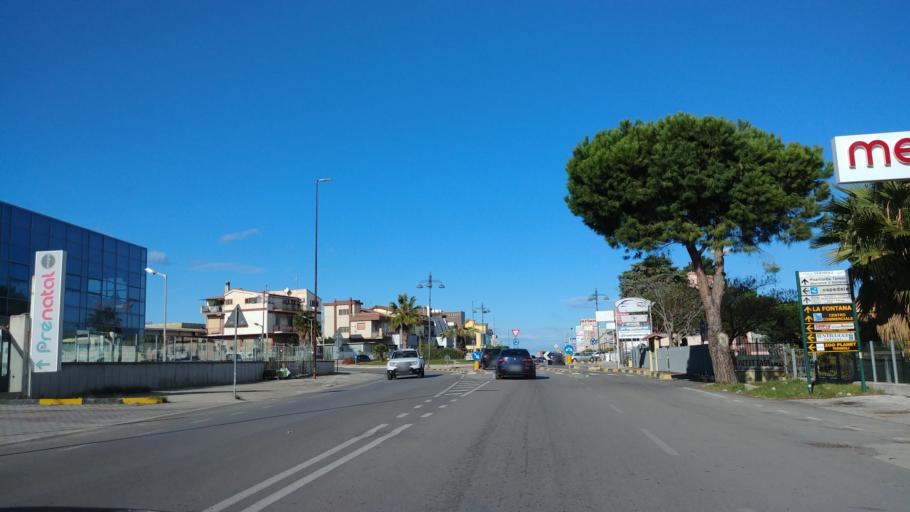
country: IT
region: Molise
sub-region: Provincia di Campobasso
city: Termoli
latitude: 41.9856
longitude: 15.0038
